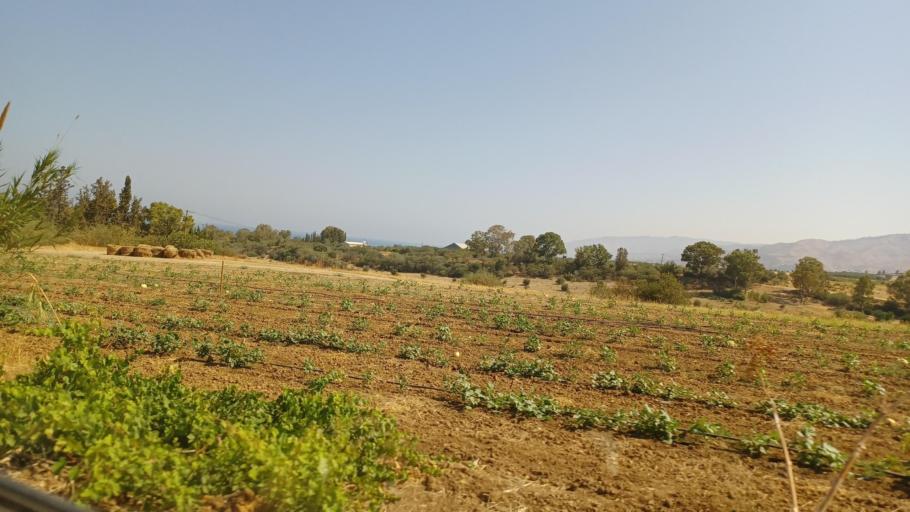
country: CY
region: Pafos
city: Polis
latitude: 35.0470
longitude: 32.4568
